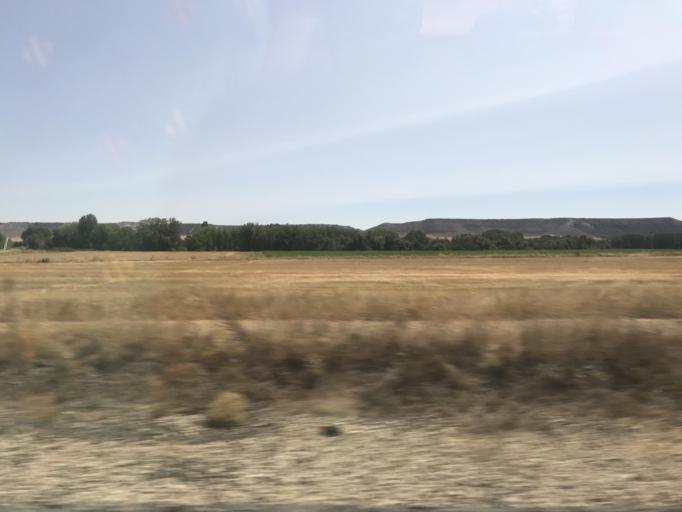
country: ES
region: Castille and Leon
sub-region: Provincia de Palencia
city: Soto de Cerrato
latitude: 41.9573
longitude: -4.4471
